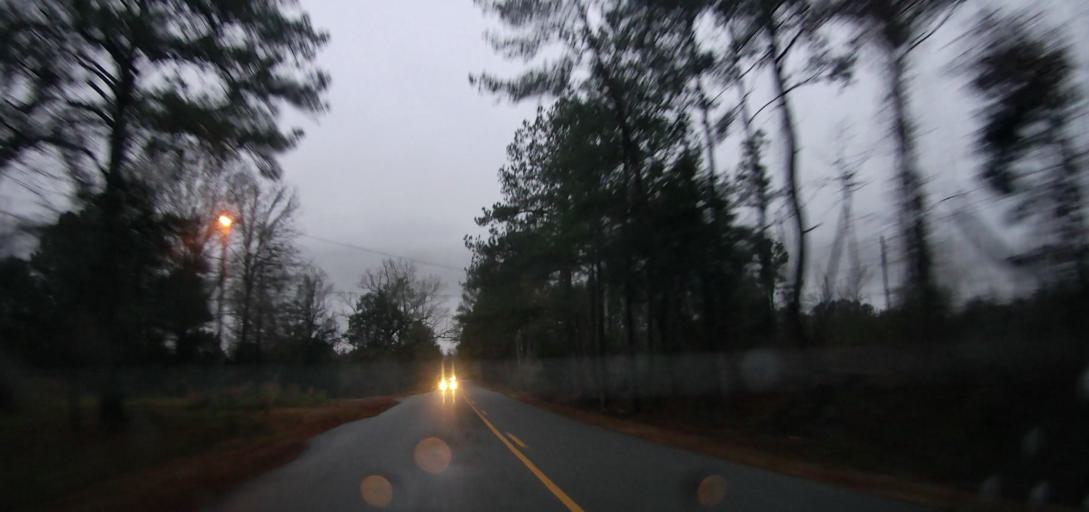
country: US
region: Alabama
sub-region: Tuscaloosa County
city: Vance
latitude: 33.1345
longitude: -87.2296
